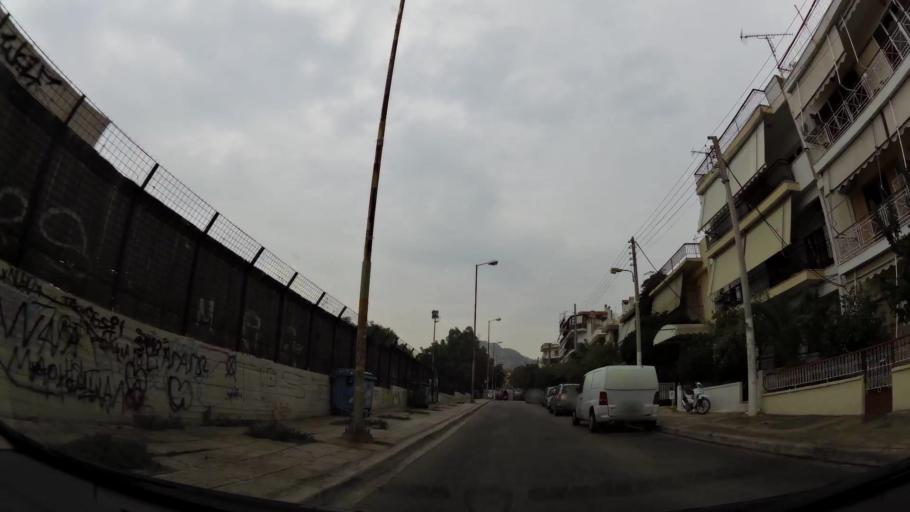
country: GR
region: Attica
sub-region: Nomos Piraios
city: Korydallos
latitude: 37.9825
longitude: 23.6519
